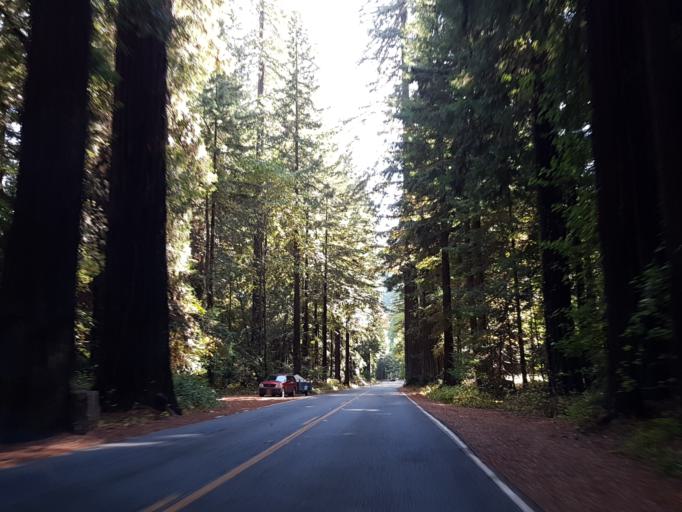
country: US
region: California
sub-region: Humboldt County
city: Rio Dell
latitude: 40.4343
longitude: -123.9850
